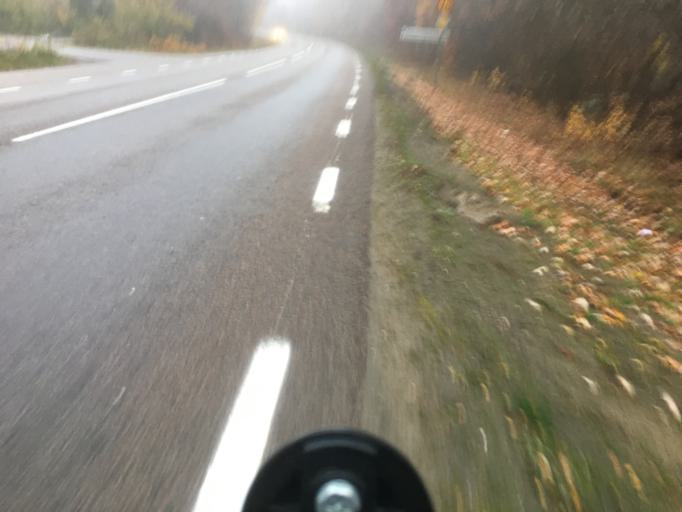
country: SE
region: Blekinge
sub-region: Karlshamns Kommun
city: Morrum
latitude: 56.1834
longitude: 14.7694
